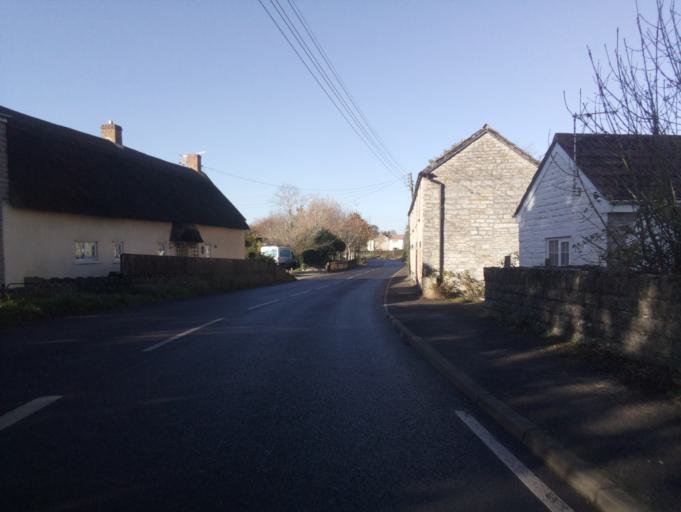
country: GB
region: England
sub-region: Somerset
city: Langport
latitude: 51.0351
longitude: -2.8099
